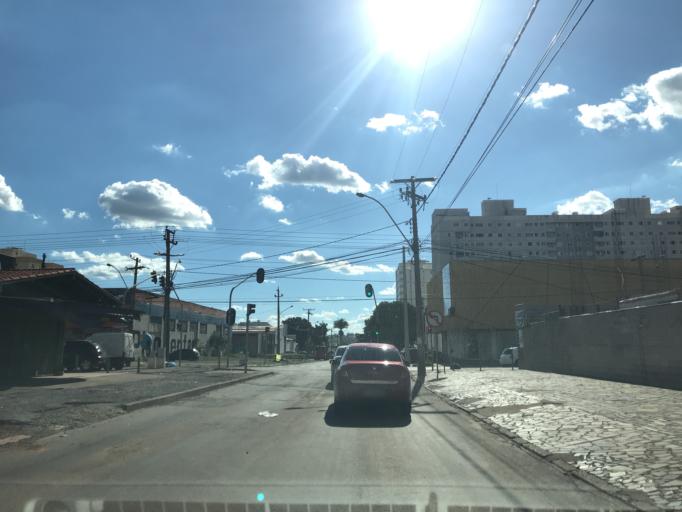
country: BR
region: Federal District
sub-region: Brasilia
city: Brasilia
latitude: -15.8063
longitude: -48.0695
